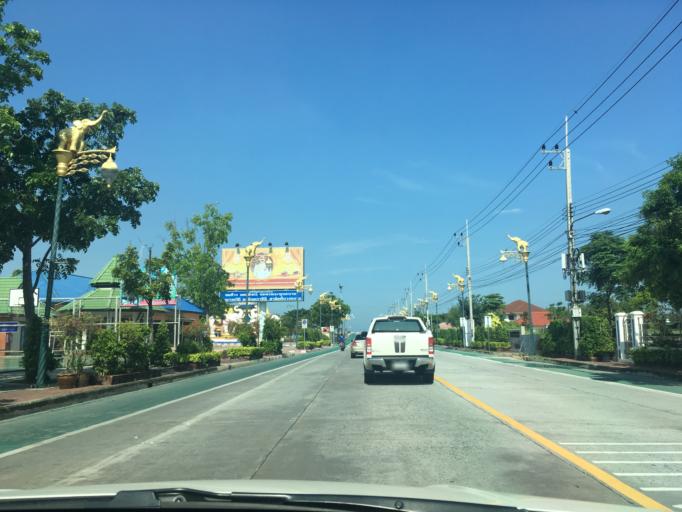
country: TH
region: Chon Buri
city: Chon Buri
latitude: 13.3856
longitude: 100.9858
